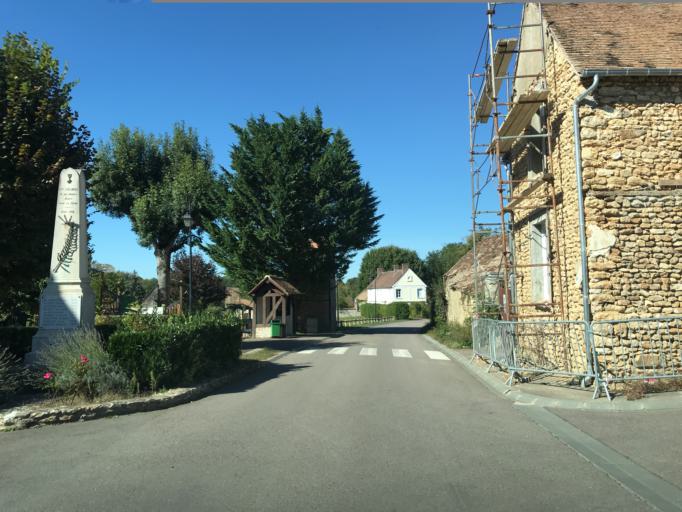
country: FR
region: Haute-Normandie
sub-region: Departement de l'Eure
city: Houlbec-Cocherel
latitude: 49.0962
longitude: 1.3372
